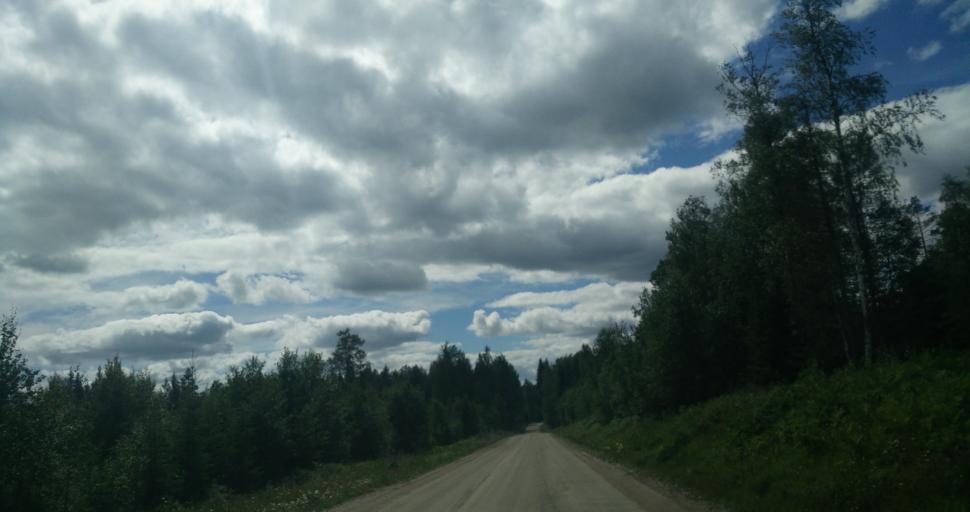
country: SE
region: Gaevleborg
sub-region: Nordanstigs Kommun
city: Bergsjoe
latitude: 62.1314
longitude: 17.1288
